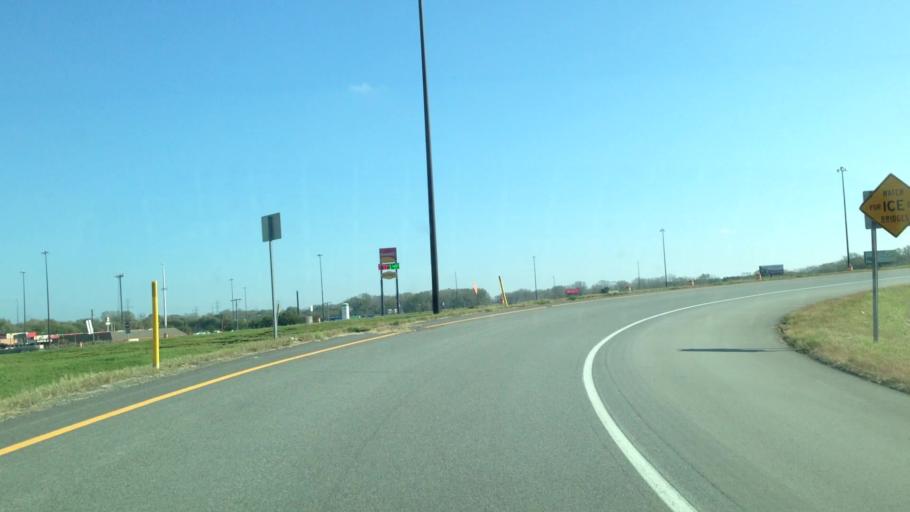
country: US
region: Indiana
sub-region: Lake County
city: Lake Station
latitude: 41.5840
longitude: -87.2415
